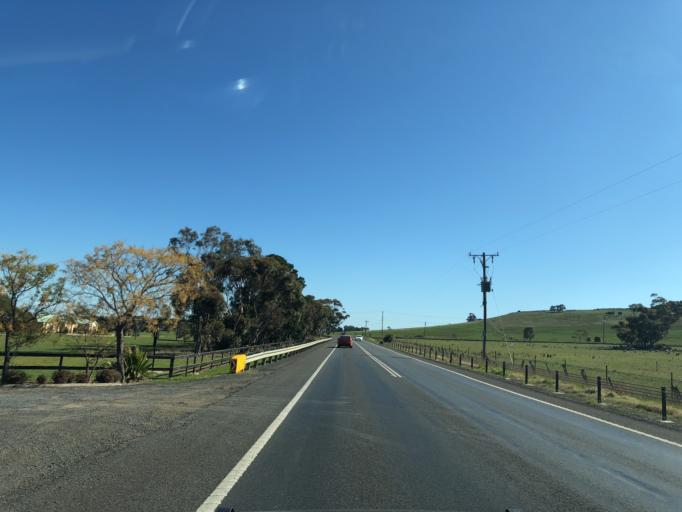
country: AU
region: Victoria
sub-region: Hume
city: Diggers Rest
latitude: -37.6244
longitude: 144.6545
